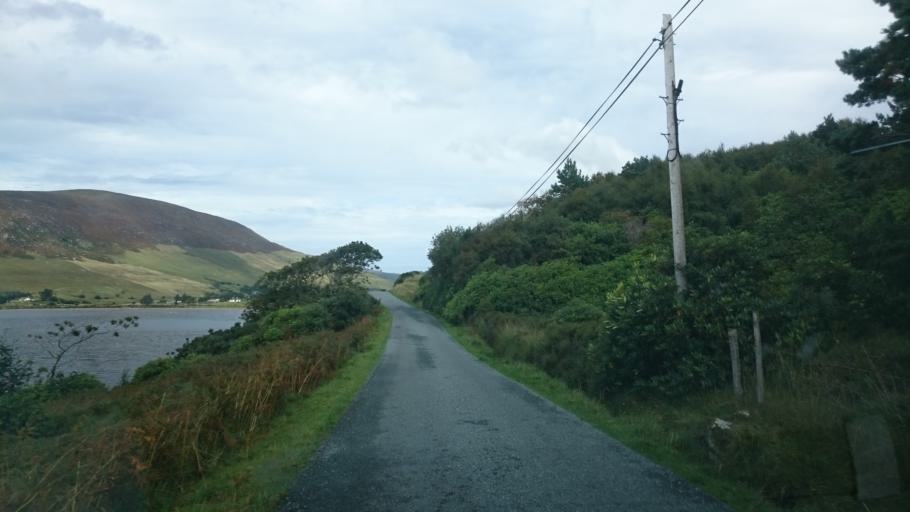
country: IE
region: Connaught
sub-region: Maigh Eo
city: Westport
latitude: 53.9529
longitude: -9.5688
